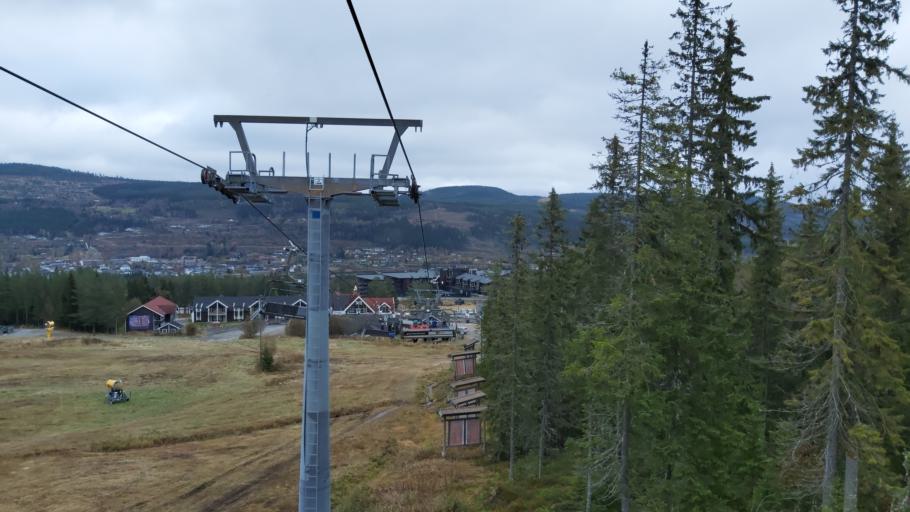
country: NO
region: Hedmark
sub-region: Trysil
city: Innbygda
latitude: 61.3080
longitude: 12.2346
